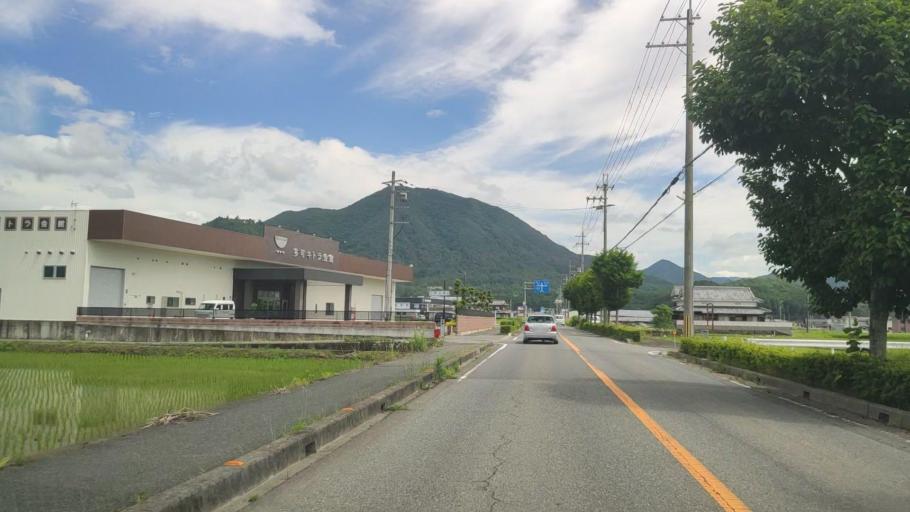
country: JP
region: Hyogo
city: Nishiwaki
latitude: 35.0640
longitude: 134.9192
